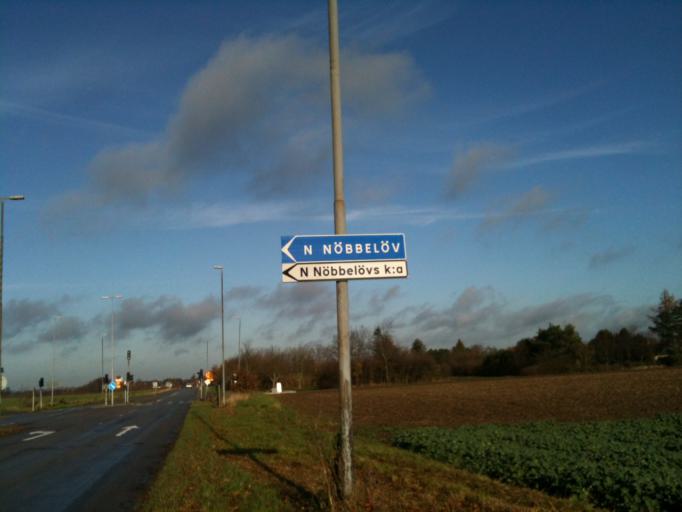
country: SE
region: Skane
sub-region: Lunds Kommun
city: Lund
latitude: 55.7332
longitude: 13.1762
